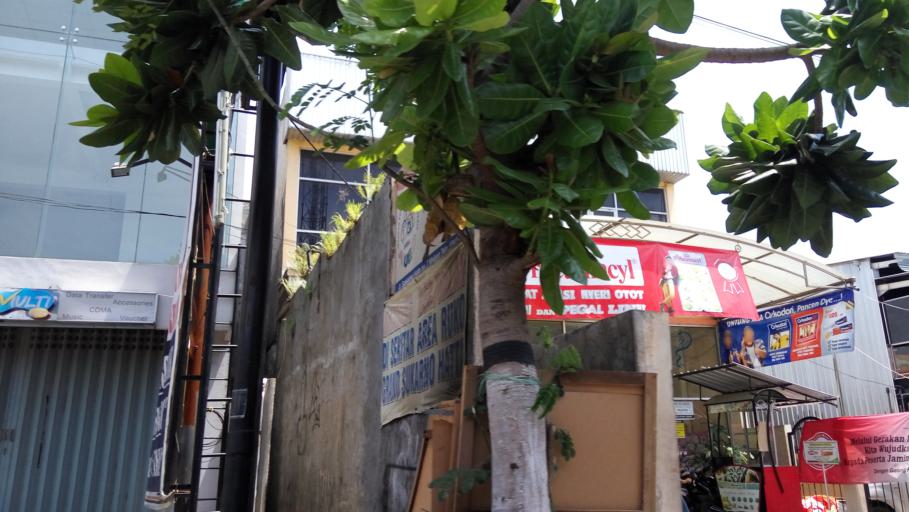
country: ID
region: East Java
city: Malang
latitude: -7.9384
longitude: 112.6293
